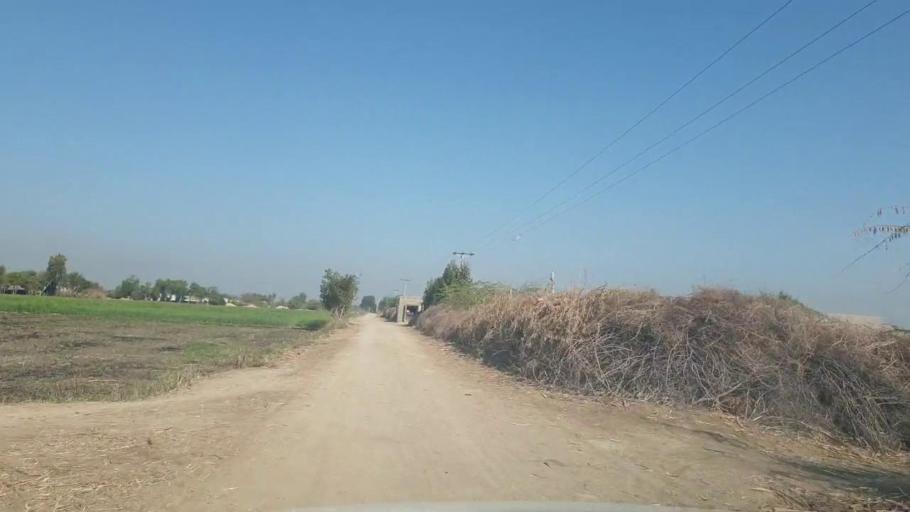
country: PK
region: Sindh
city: Mirpur Khas
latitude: 25.5041
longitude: 69.1584
